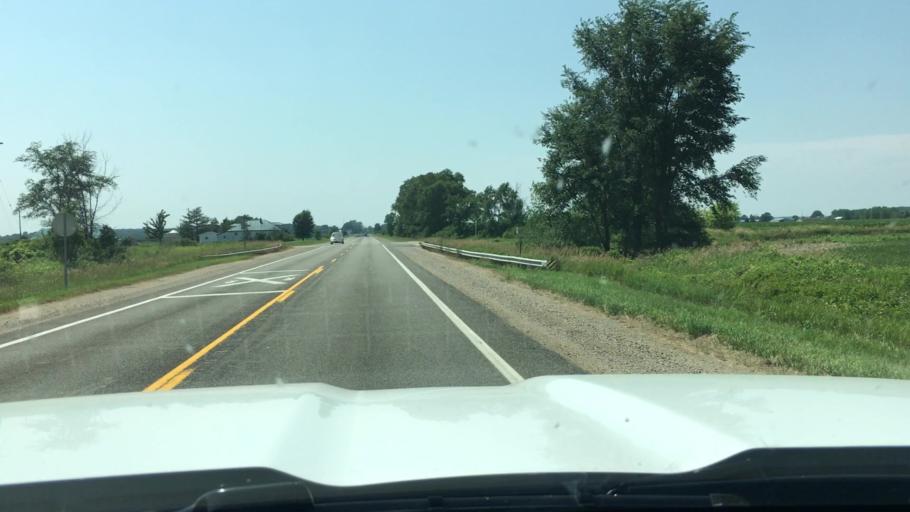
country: US
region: Michigan
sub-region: Gratiot County
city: Ithaca
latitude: 43.1758
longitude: -84.4662
